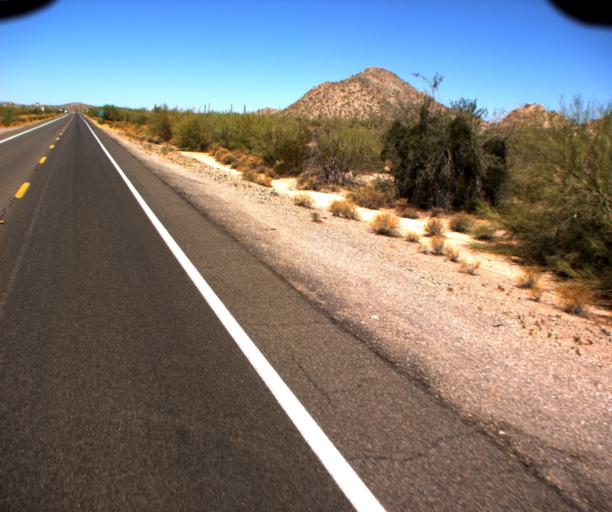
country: US
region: Arizona
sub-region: Pinal County
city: Maricopa
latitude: 32.8383
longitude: -112.1223
